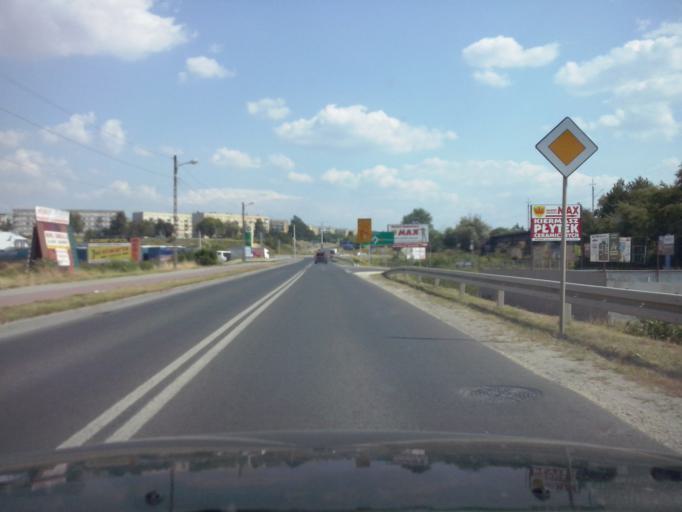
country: PL
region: Swietokrzyskie
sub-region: Powiat staszowski
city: Staszow
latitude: 50.5559
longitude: 21.1715
